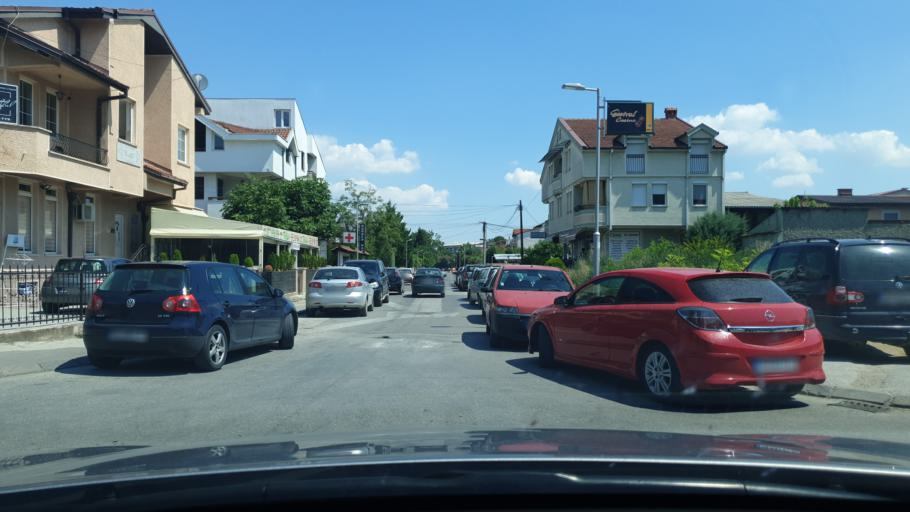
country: MK
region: Kisela Voda
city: Kisela Voda
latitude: 41.9394
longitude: 21.5157
